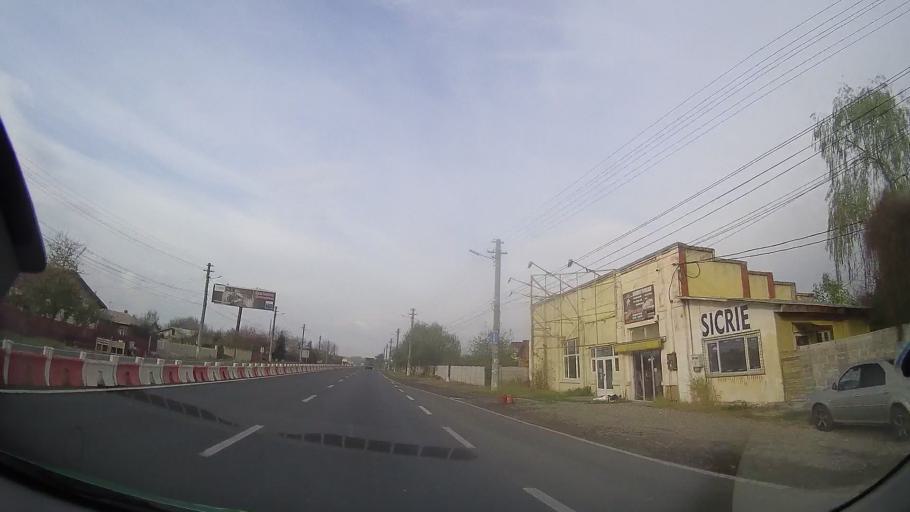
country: RO
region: Prahova
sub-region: Comuna Gorgota
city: Potigrafu
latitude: 44.7866
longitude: 26.0982
